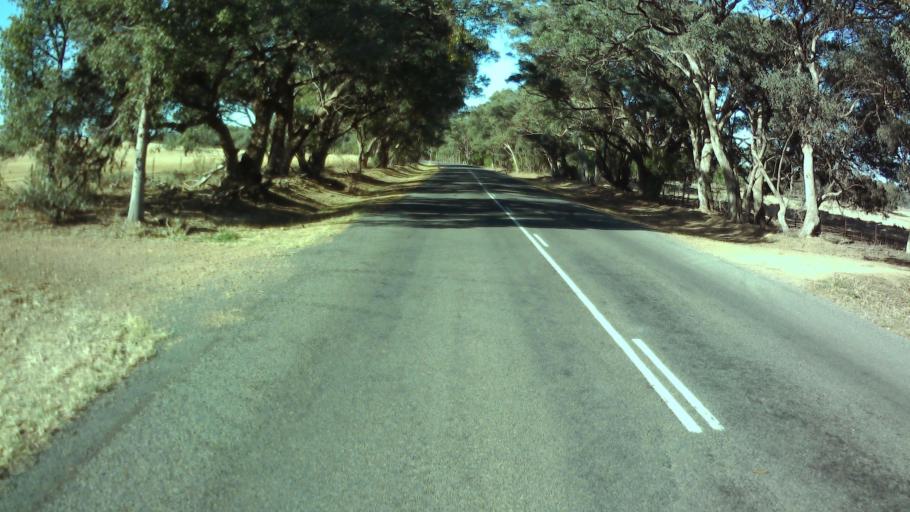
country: AU
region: New South Wales
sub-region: Weddin
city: Grenfell
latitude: -33.9922
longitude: 148.1351
